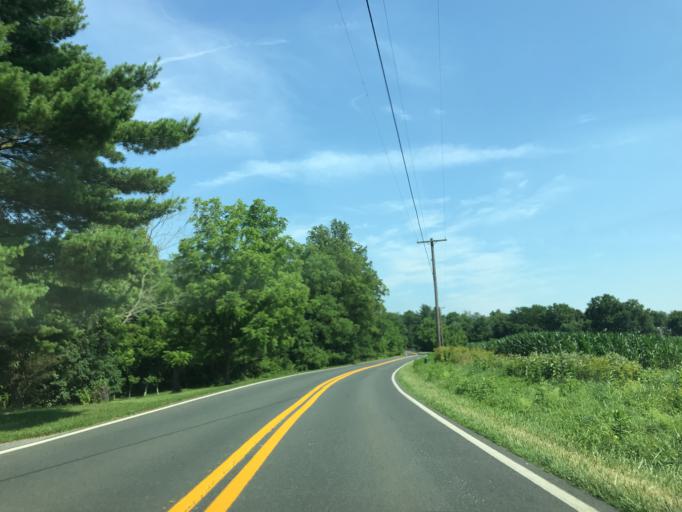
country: US
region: Maryland
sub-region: Carroll County
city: Taneytown
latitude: 39.6274
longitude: -77.1442
